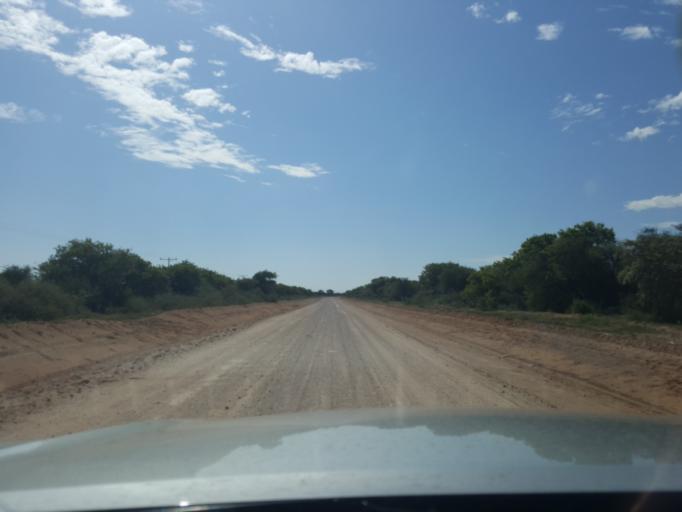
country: BW
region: Kweneng
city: Khudumelapye
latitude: -23.7951
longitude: 24.7947
